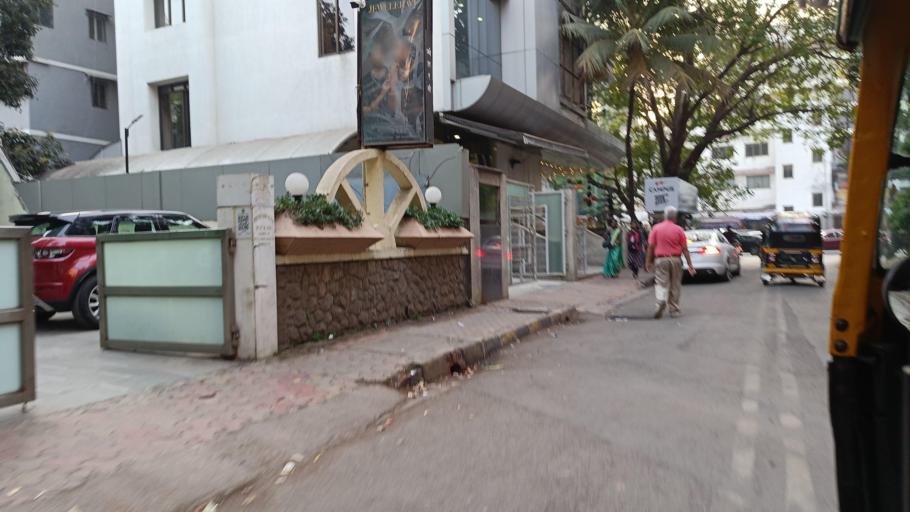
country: IN
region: Maharashtra
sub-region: Mumbai Suburban
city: Mumbai
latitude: 19.0701
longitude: 72.8345
